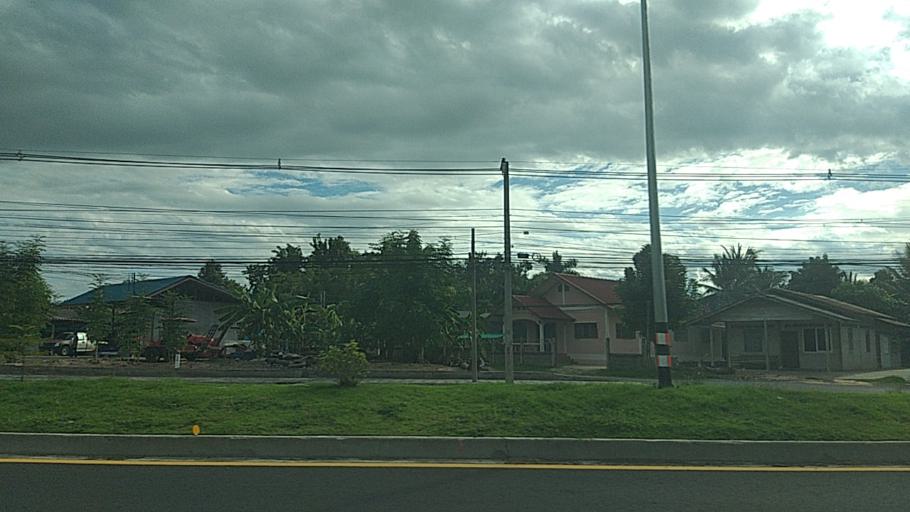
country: TH
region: Surin
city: Prasat
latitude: 14.6188
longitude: 103.4142
